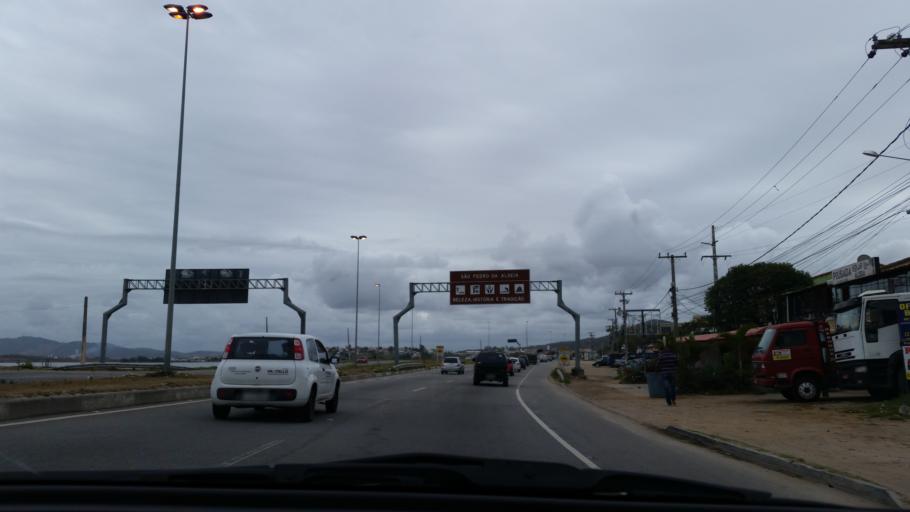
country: BR
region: Rio de Janeiro
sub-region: Sao Pedro Da Aldeia
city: Sao Pedro da Aldeia
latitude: -22.8558
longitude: -42.0601
